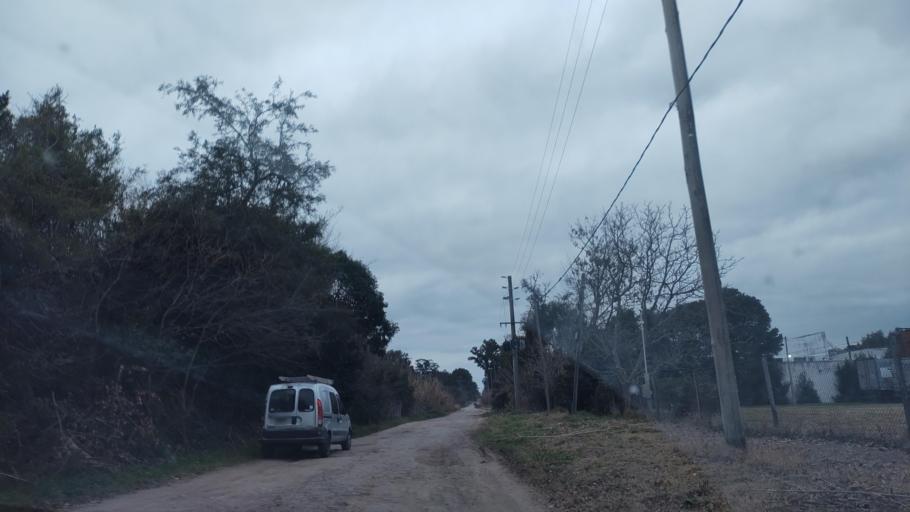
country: AR
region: Buenos Aires
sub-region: Partido de La Plata
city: La Plata
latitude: -34.8650
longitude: -58.1204
